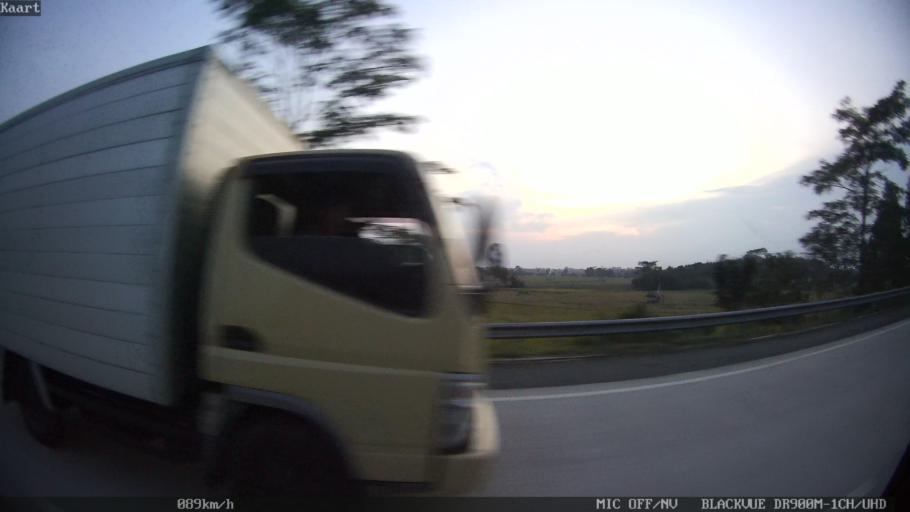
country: ID
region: Lampung
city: Sidorejo
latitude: -5.6019
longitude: 105.5541
